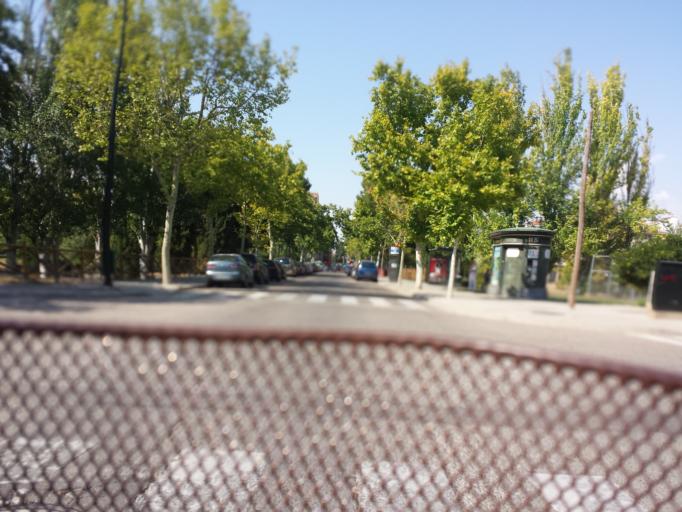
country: ES
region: Aragon
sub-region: Provincia de Zaragoza
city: Zaragoza
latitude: 41.6429
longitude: -0.8625
